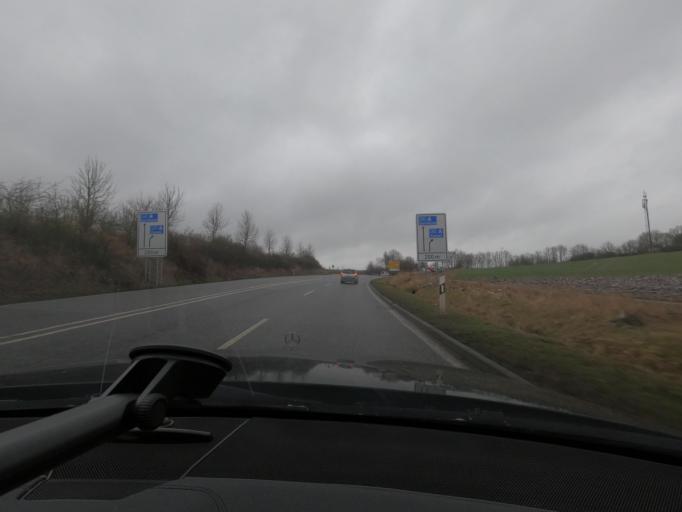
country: DE
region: Hesse
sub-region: Regierungsbezirk Kassel
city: Martinhagen
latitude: 51.3184
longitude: 9.2794
